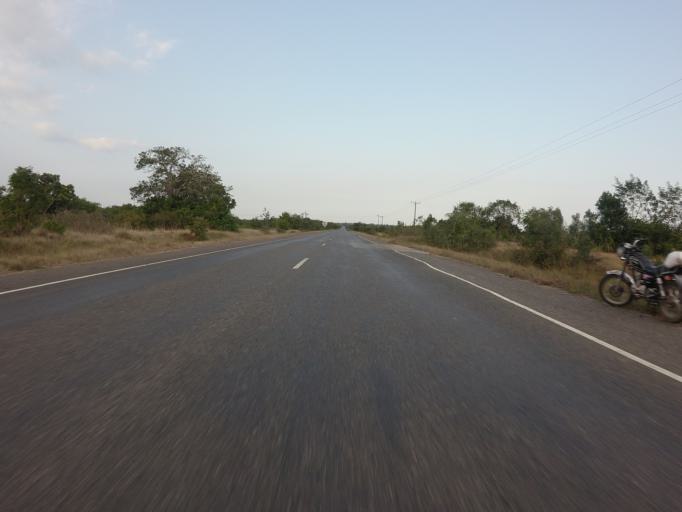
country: GH
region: Volta
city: Anloga
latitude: 6.0792
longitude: 0.5845
